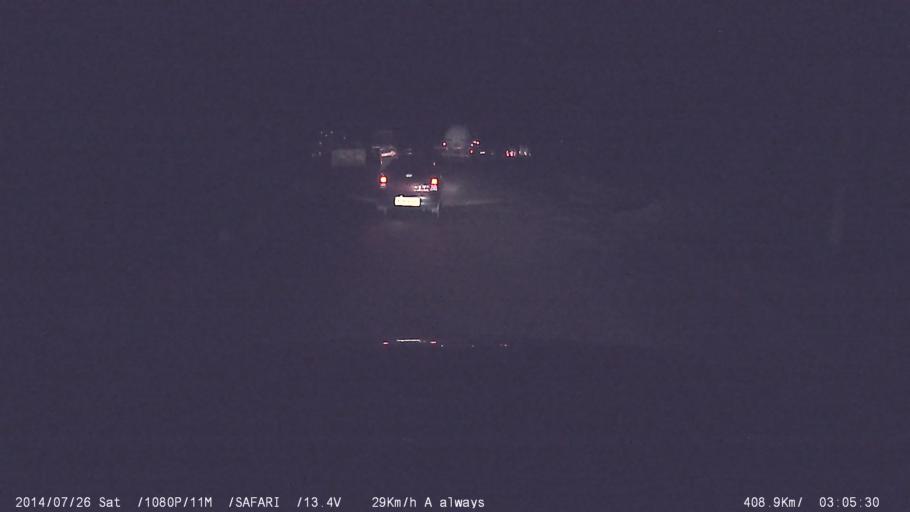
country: IN
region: Kerala
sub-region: Palakkad district
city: Palakkad
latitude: 10.7032
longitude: 76.5928
